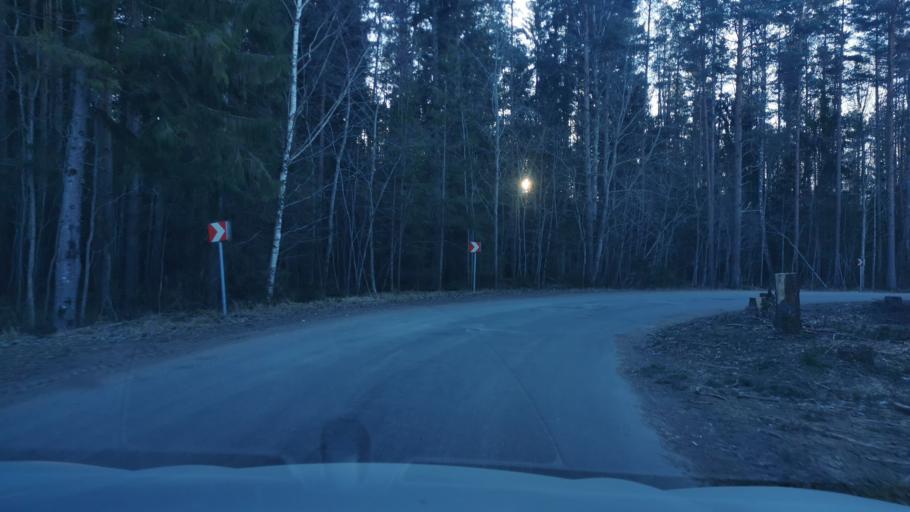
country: EE
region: Ida-Virumaa
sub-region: Kohtla-Nomme vald
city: Kohtla-Nomme
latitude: 59.3493
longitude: 27.1774
